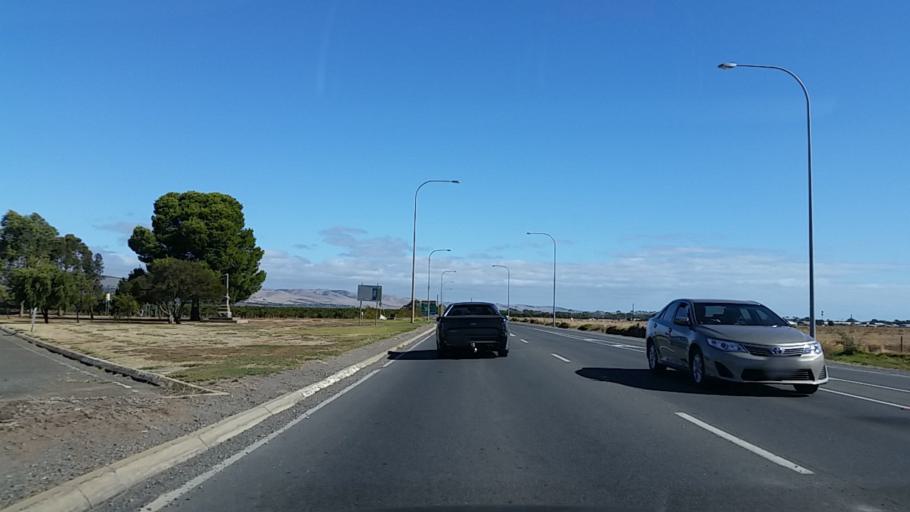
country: AU
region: South Australia
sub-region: Onkaparinga
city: Aldinga
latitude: -35.2701
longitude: 138.4833
